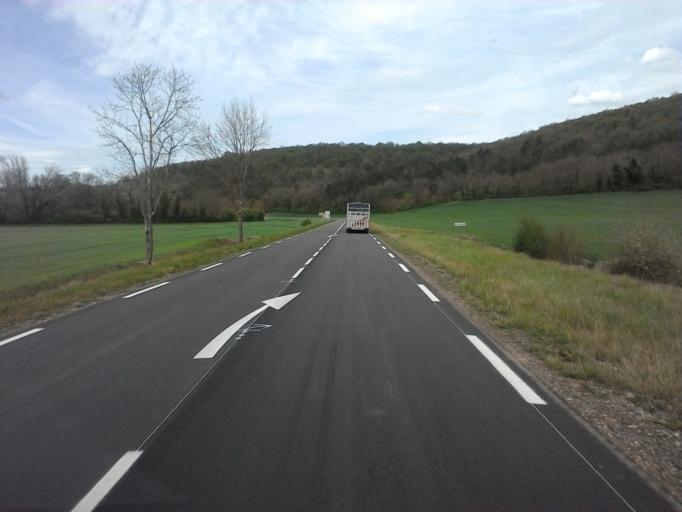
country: FR
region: Bourgogne
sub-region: Departement de l'Yonne
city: Joux-la-Ville
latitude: 47.5721
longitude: 3.7825
